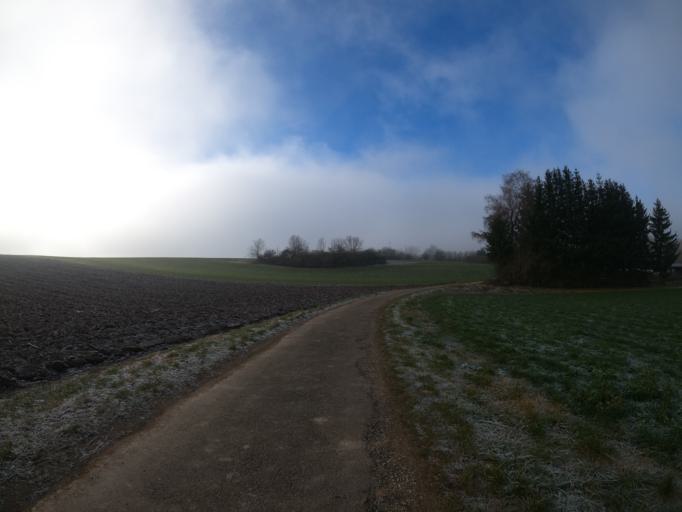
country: DE
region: Baden-Wuerttemberg
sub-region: Regierungsbezirk Stuttgart
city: Bad Uberkingen
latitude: 48.5856
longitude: 9.7757
